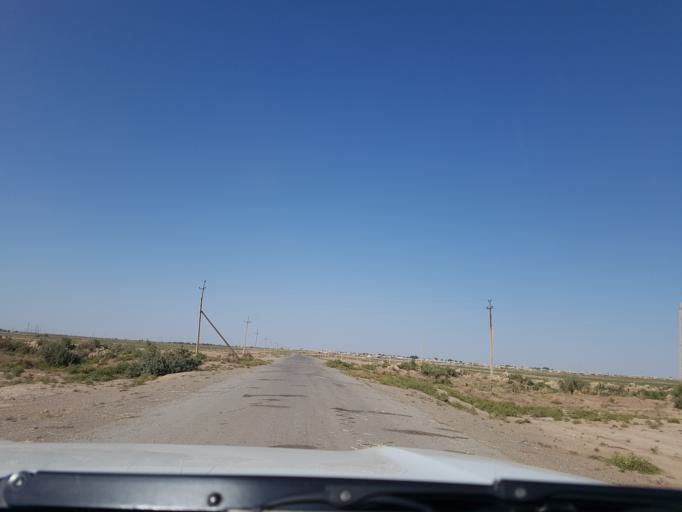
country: IR
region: Razavi Khorasan
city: Sarakhs
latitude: 36.4971
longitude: 61.2537
